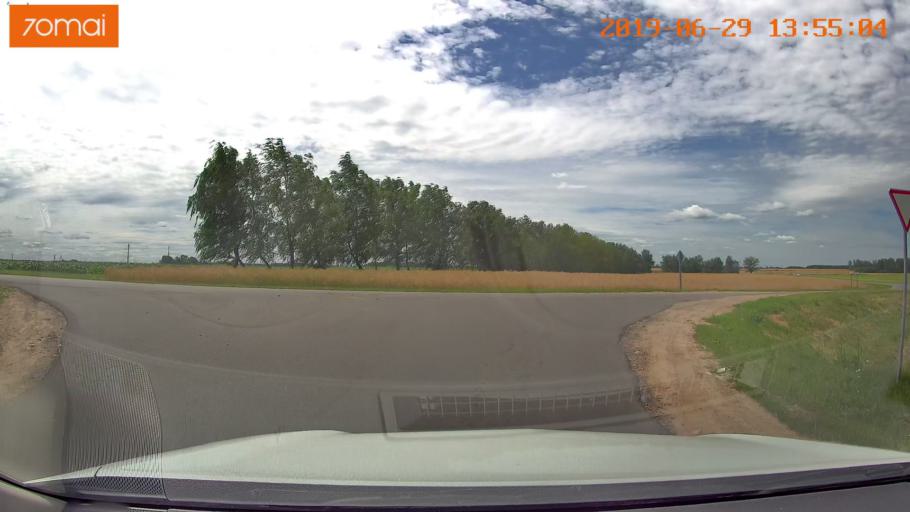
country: BY
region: Minsk
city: Slutsk
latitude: 52.9830
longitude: 27.5251
